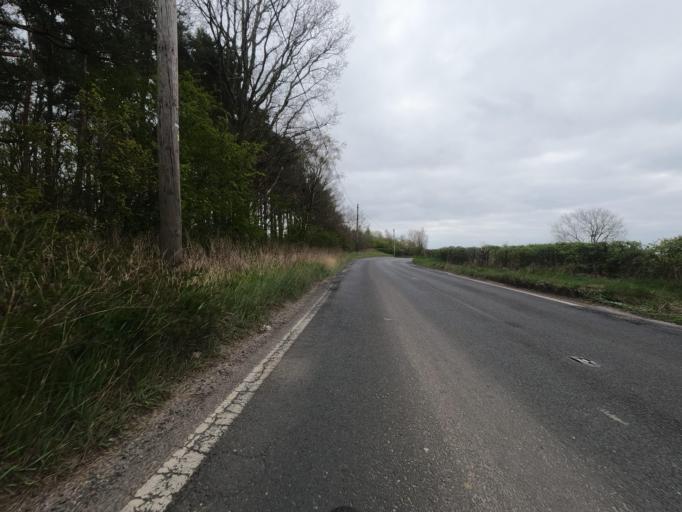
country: GB
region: England
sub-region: Newcastle upon Tyne
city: Dinnington
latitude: 55.0648
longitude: -1.6850
